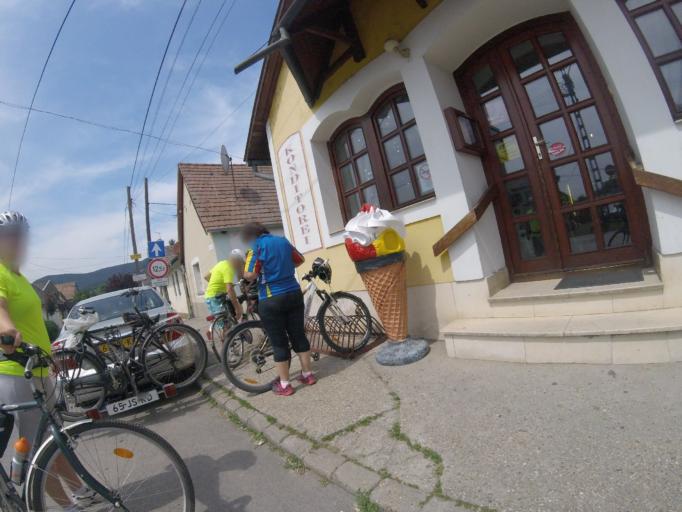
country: HU
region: Pest
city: Tahitotfalu
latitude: 47.7547
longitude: 19.0875
